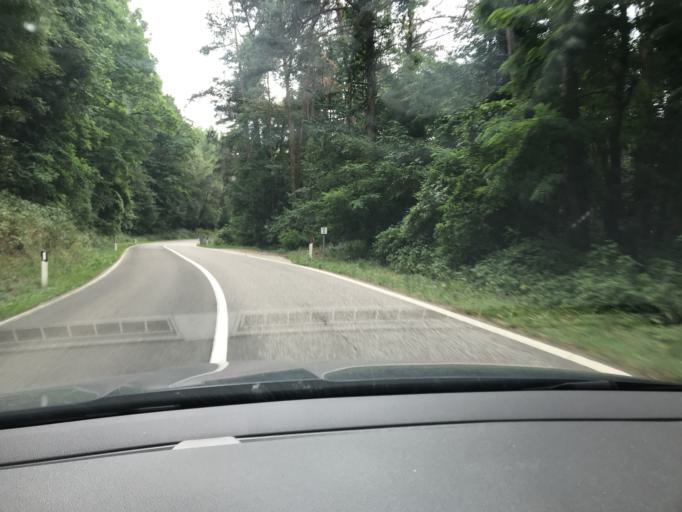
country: IT
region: Trentino-Alto Adige
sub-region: Bolzano
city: Ponte Gardena
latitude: 46.6104
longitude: 11.5436
